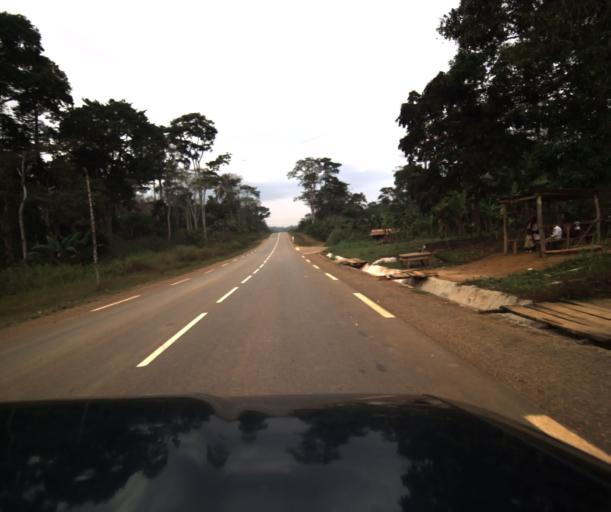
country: CM
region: Centre
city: Akono
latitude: 3.6295
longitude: 11.3231
